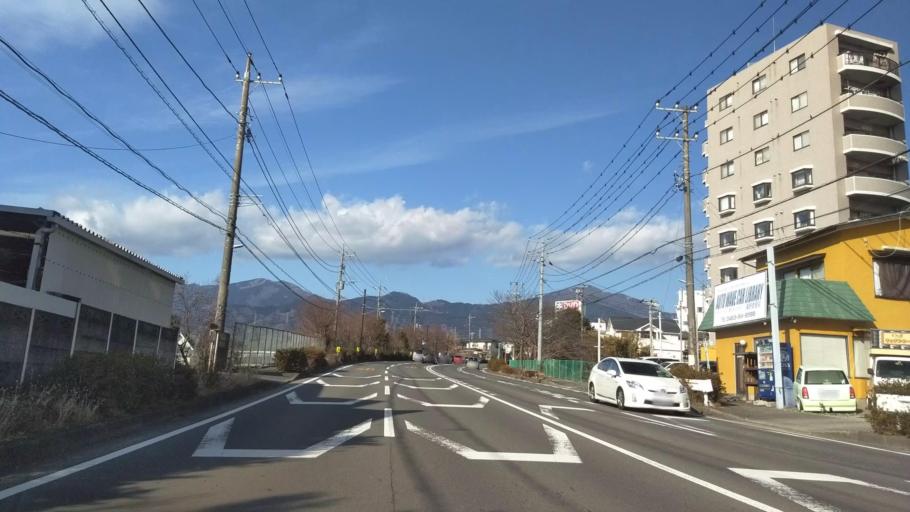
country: JP
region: Kanagawa
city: Hadano
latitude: 35.3724
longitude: 139.2353
